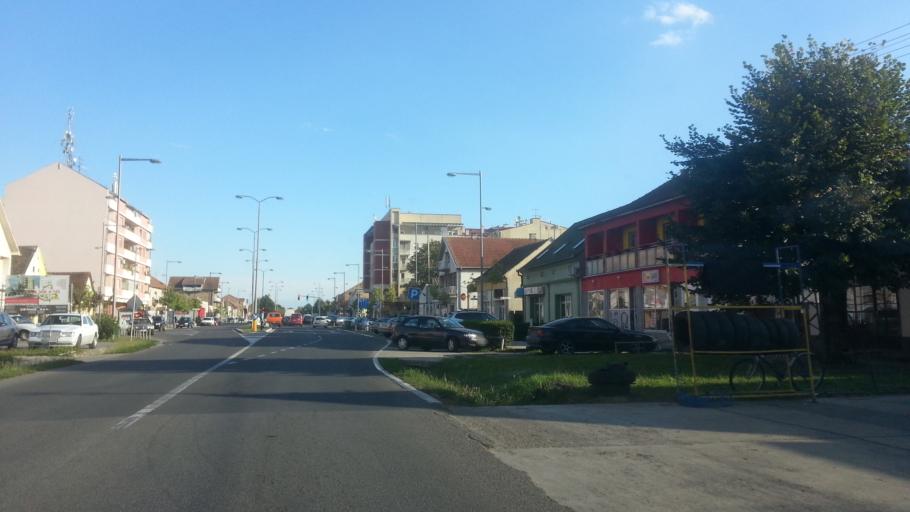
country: RS
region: Autonomna Pokrajina Vojvodina
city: Nova Pazova
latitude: 44.9456
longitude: 20.2174
